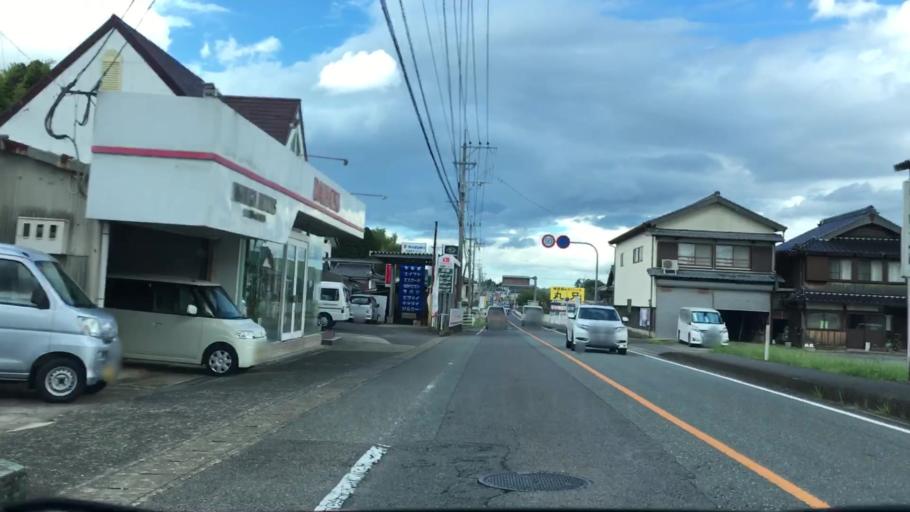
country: JP
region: Saga Prefecture
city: Imaricho-ko
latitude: 33.1981
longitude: 129.8505
